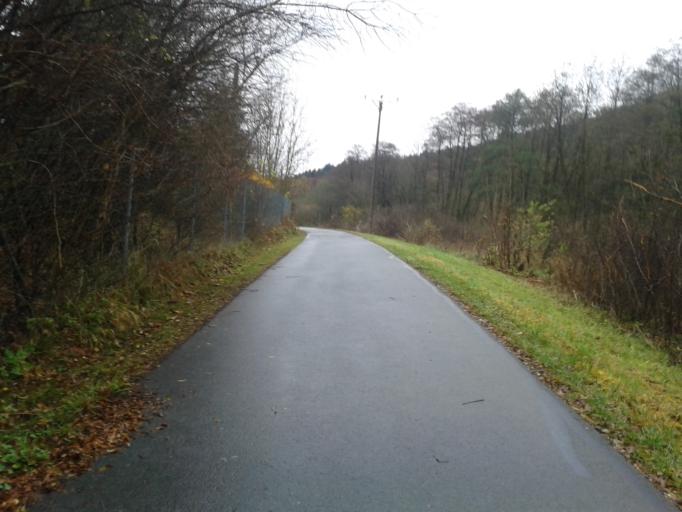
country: DE
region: Bavaria
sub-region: Regierungsbezirk Mittelfranken
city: Pommelsbrunn
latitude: 49.4996
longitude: 11.5226
